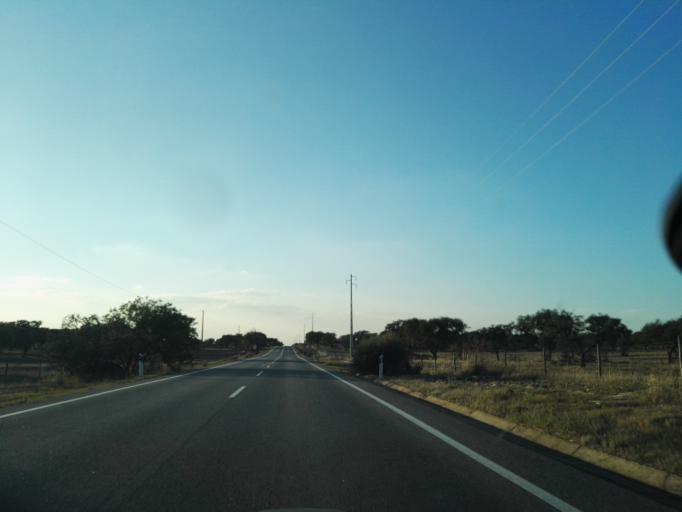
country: PT
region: Evora
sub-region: Arraiolos
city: Arraiolos
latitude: 38.8550
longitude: -7.9112
